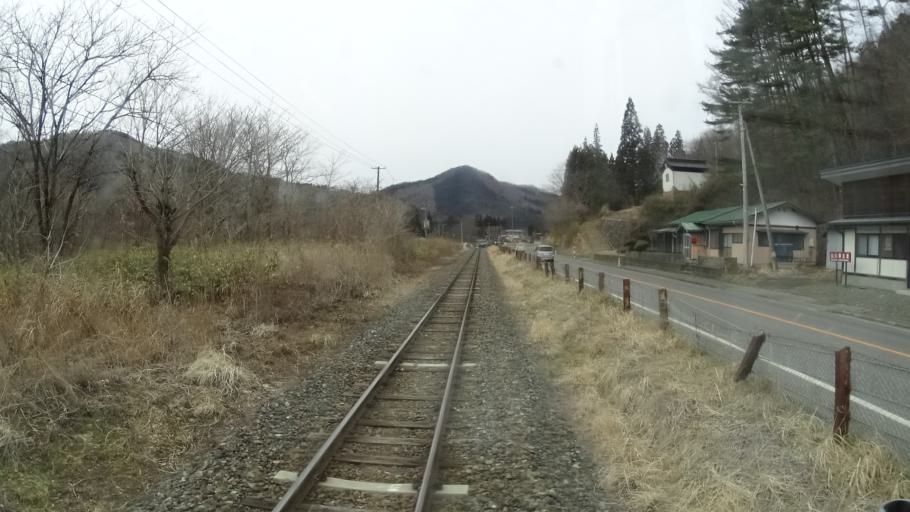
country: JP
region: Iwate
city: Hanamaki
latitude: 39.3553
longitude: 141.3162
